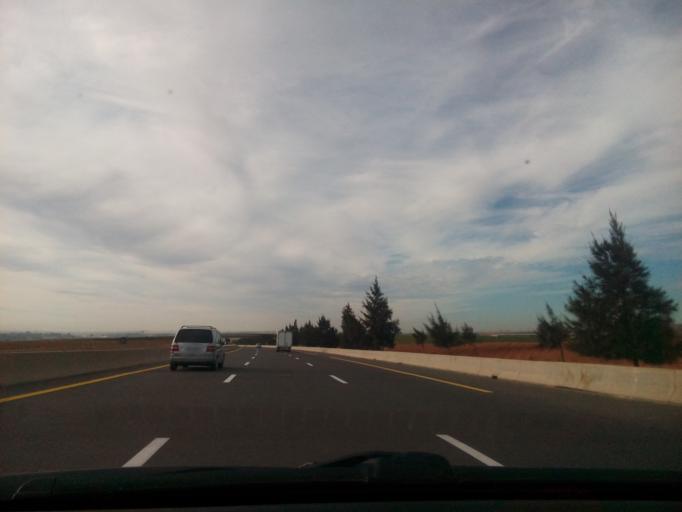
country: DZ
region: Sidi Bel Abbes
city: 'Ain el Berd
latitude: 35.3225
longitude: -0.5396
